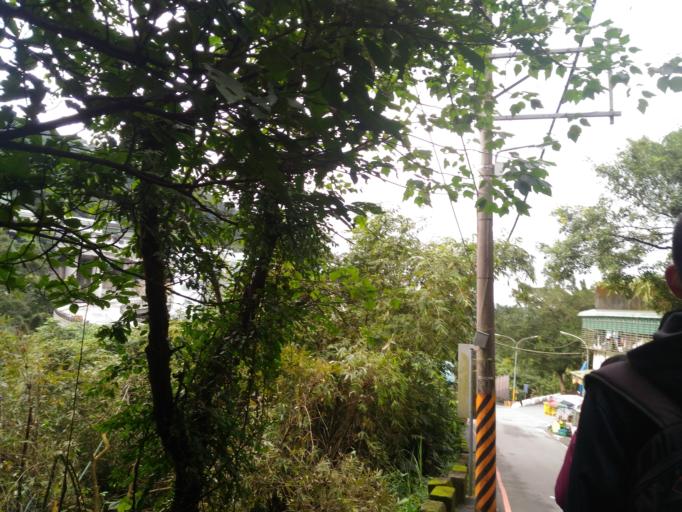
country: TW
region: Taipei
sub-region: Taipei
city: Banqiao
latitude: 24.9508
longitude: 121.4482
